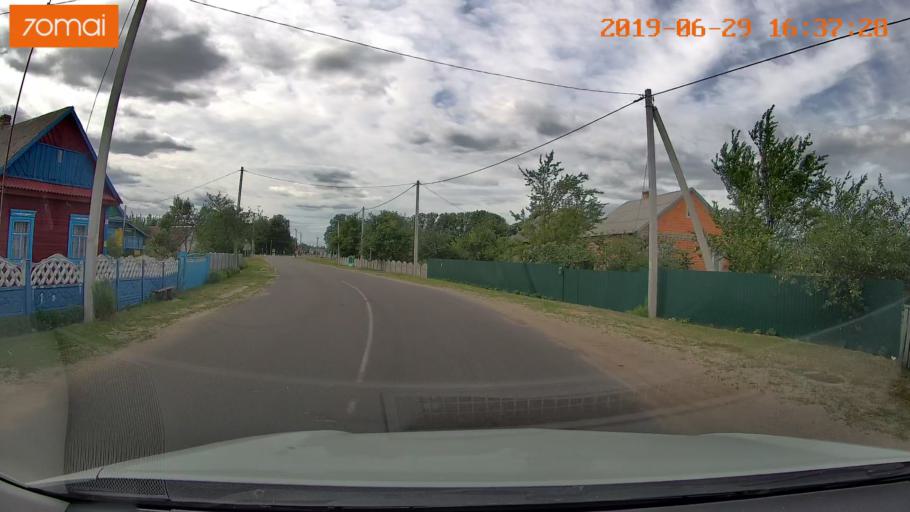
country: BY
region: Brest
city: Luninyets
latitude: 52.2278
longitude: 27.0215
